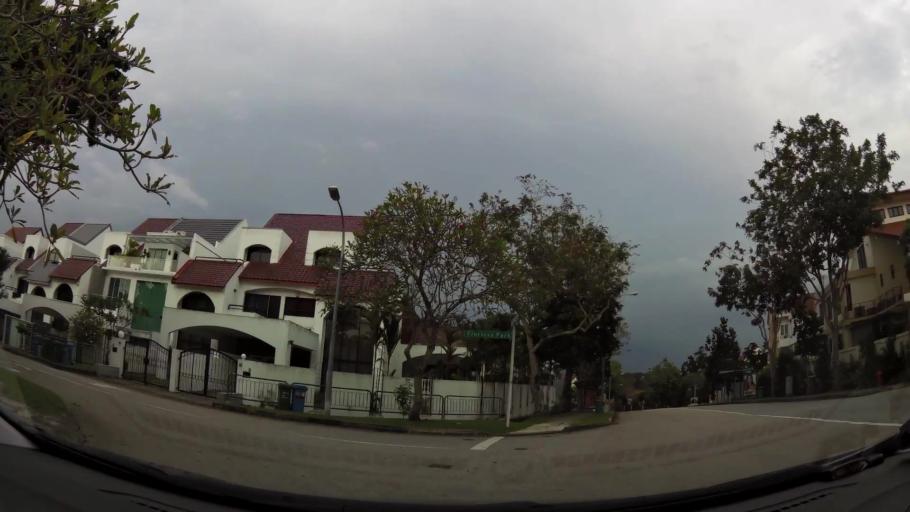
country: MY
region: Johor
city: Kampung Pasir Gudang Baru
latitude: 1.3867
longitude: 103.8368
